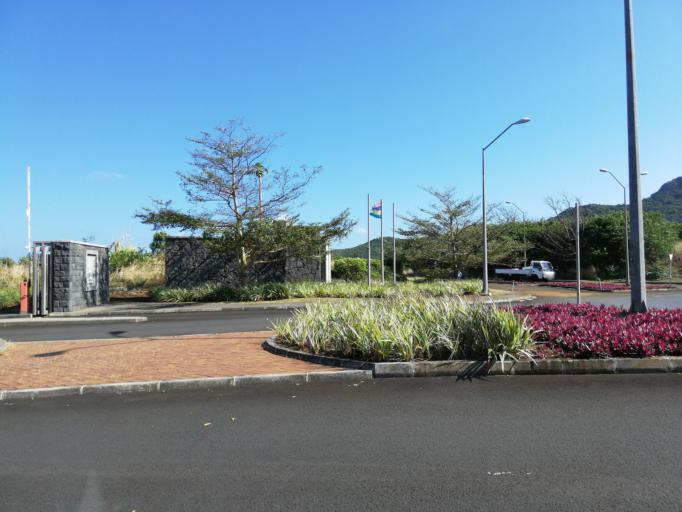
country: MU
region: Moka
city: Moka
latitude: -20.2220
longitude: 57.4933
